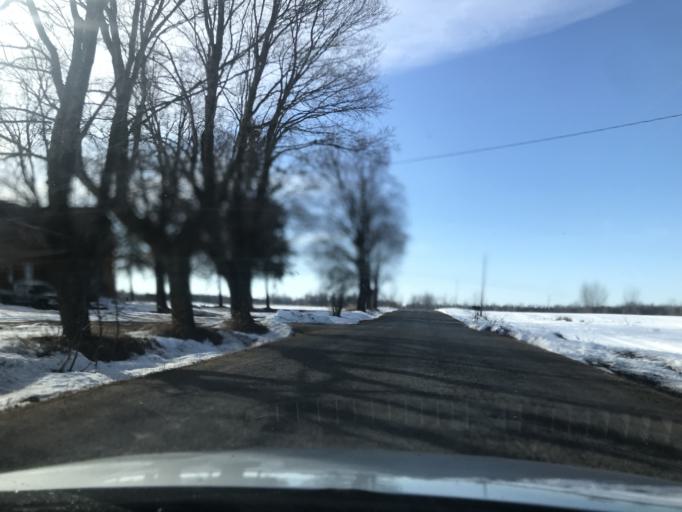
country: US
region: Wisconsin
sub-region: Oconto County
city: Oconto Falls
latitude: 44.9402
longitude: -88.0167
